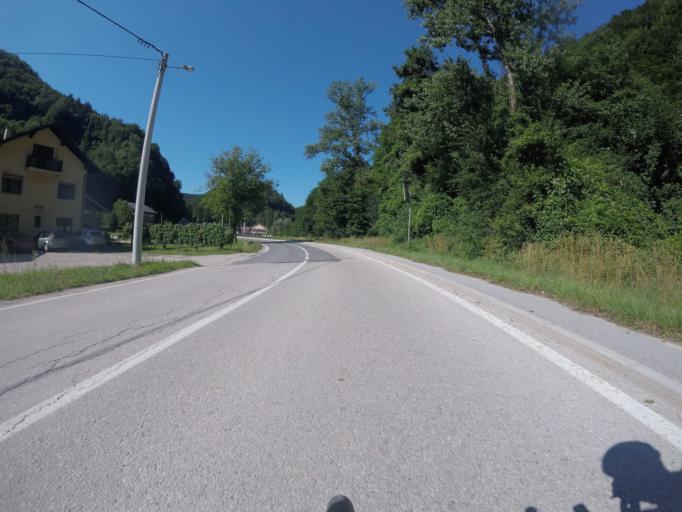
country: HR
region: Zagrebacka
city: Bregana
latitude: 45.8231
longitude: 15.6448
